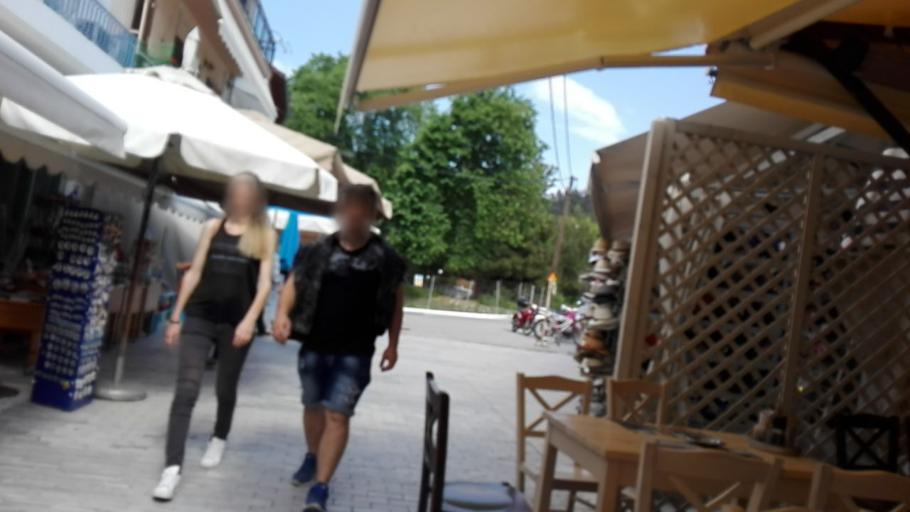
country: GR
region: East Macedonia and Thrace
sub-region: Nomos Kavalas
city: Thasos
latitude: 40.7805
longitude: 24.7113
